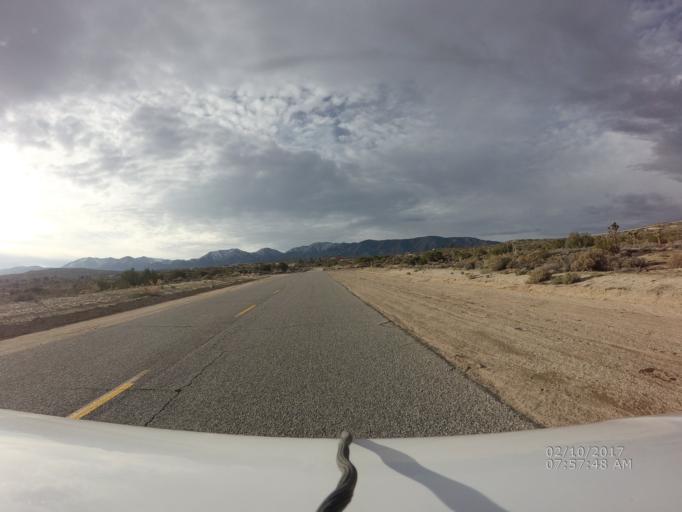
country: US
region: California
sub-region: Los Angeles County
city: Littlerock
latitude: 34.4927
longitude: -117.9072
